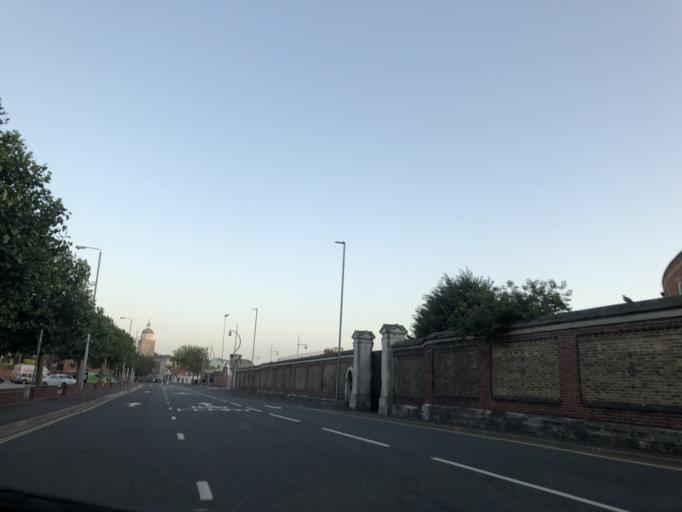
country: GB
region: England
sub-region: Portsmouth
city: Portsmouth
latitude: 50.7940
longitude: -1.1044
